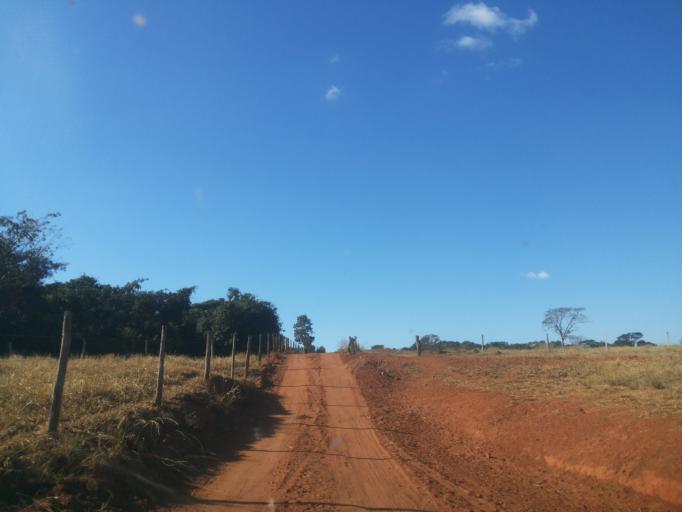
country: BR
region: Minas Gerais
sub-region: Centralina
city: Centralina
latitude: -18.7272
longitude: -49.1575
